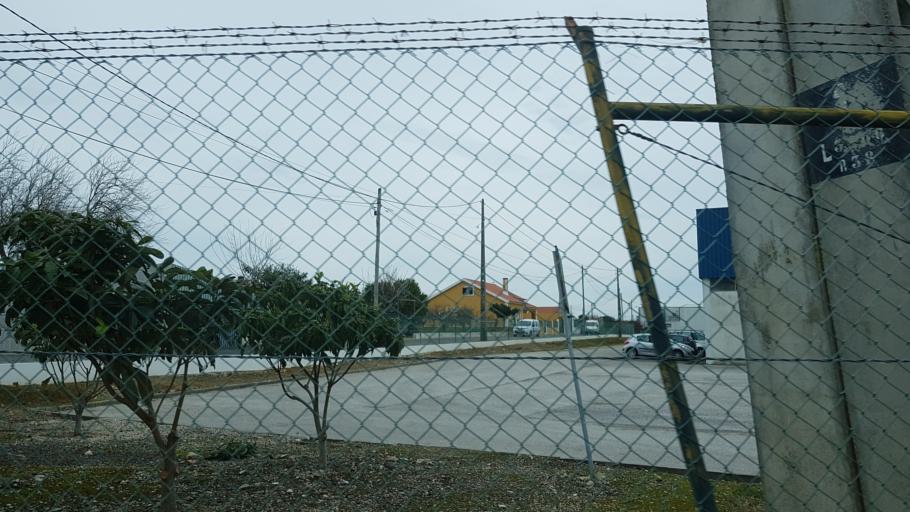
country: PT
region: Lisbon
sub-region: Alenquer
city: Carregado
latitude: 39.0346
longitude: -8.9645
